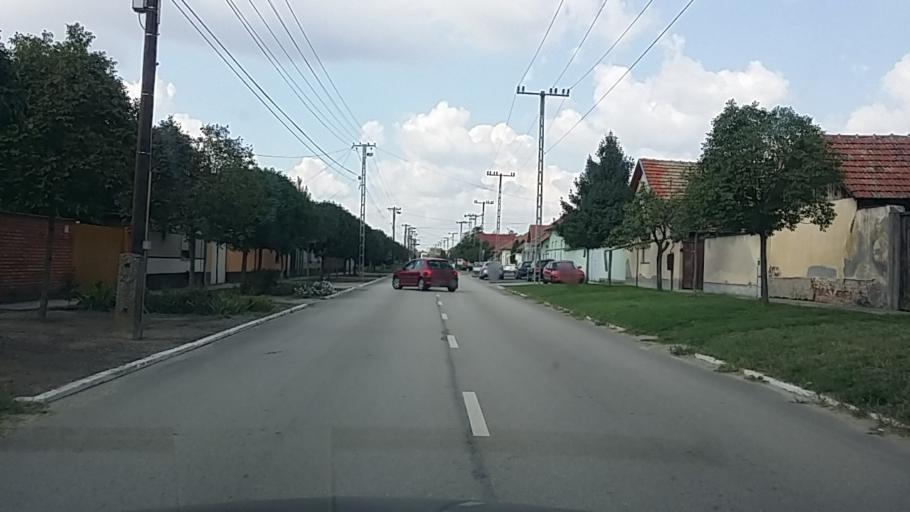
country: HU
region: Bacs-Kiskun
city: Tiszaalpar
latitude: 46.8181
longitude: 19.9957
